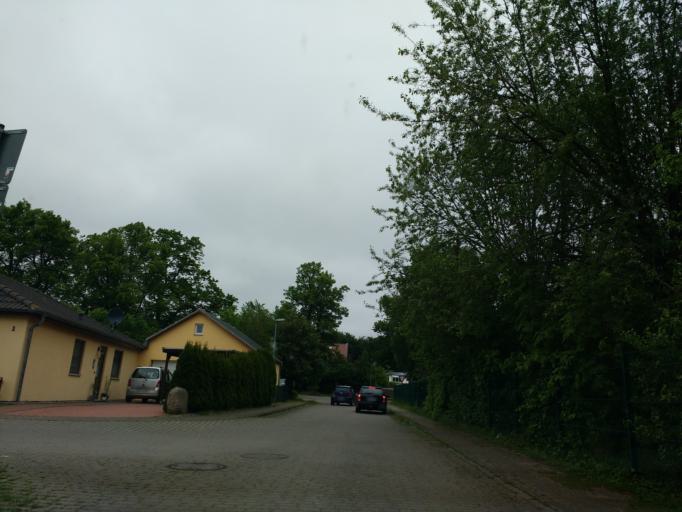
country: DE
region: Mecklenburg-Vorpommern
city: Neukloster
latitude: 53.8653
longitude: 11.6973
